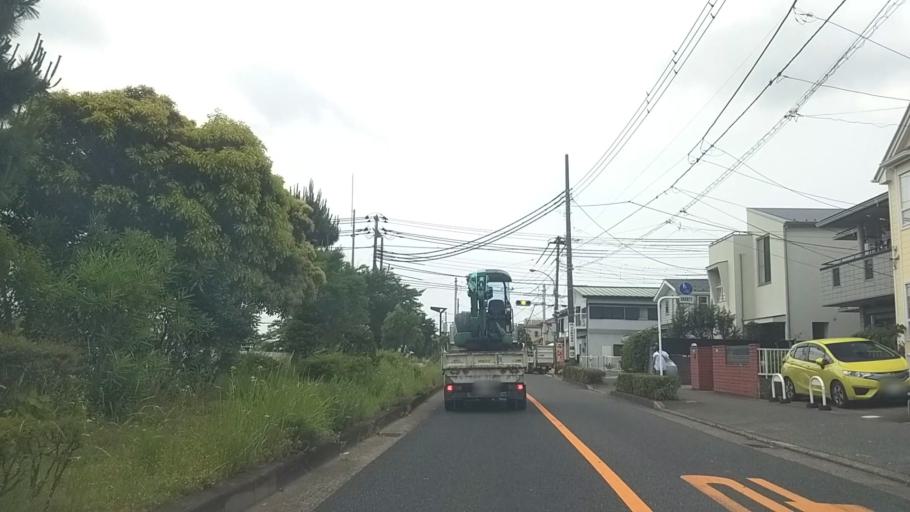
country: JP
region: Kanagawa
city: Fujisawa
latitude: 35.3296
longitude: 139.4645
